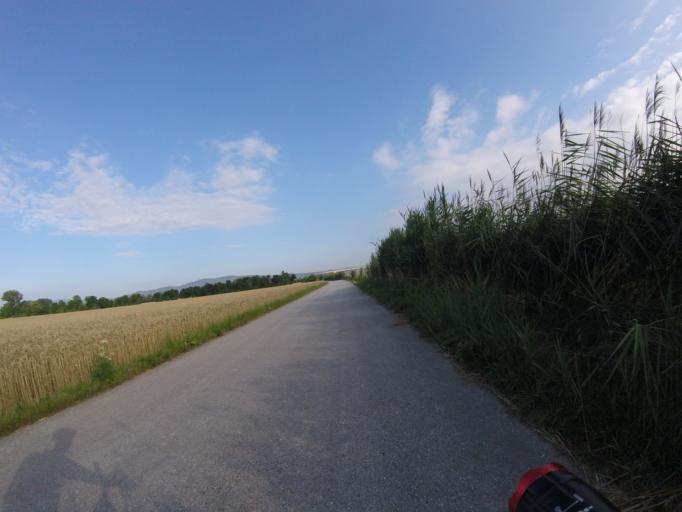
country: AT
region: Lower Austria
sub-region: Politischer Bezirk Modling
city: Munchendorf
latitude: 48.0186
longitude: 16.3591
